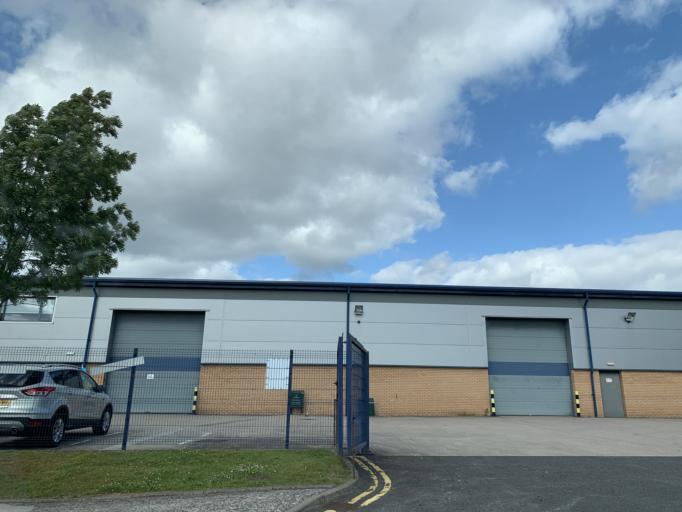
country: GB
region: Scotland
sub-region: Renfrewshire
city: Renfrew
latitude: 55.8573
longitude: -4.3728
